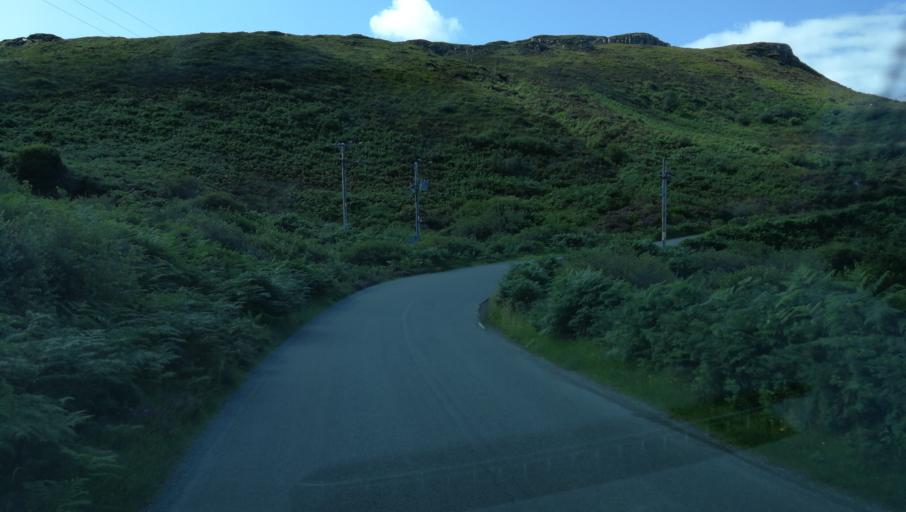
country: GB
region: Scotland
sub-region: Highland
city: Isle of Skye
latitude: 57.4508
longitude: -6.6635
